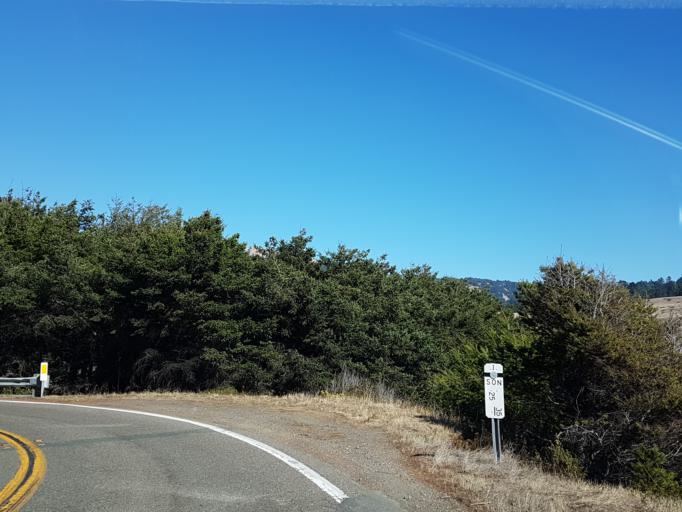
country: US
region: California
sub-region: Sonoma County
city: Monte Rio
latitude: 38.4719
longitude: -123.1568
